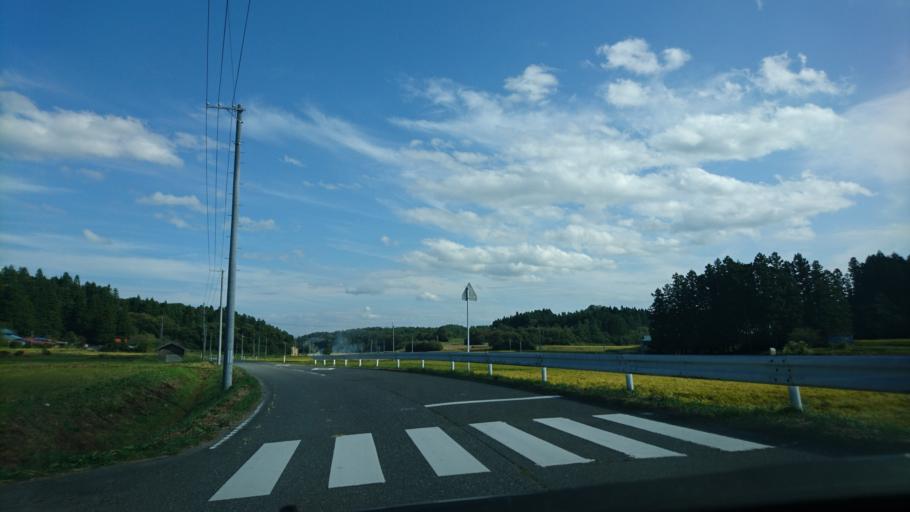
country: JP
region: Iwate
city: Ichinoseki
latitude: 38.8760
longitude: 141.0719
